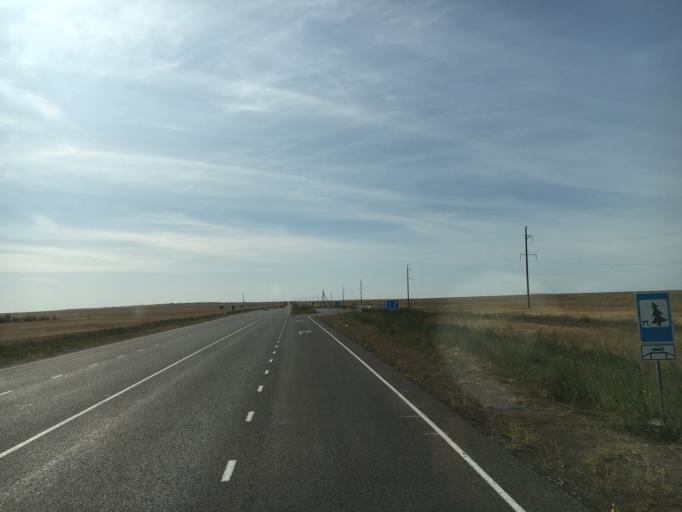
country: KZ
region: Batys Qazaqstan
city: Peremetnoe
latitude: 51.1172
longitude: 50.6262
